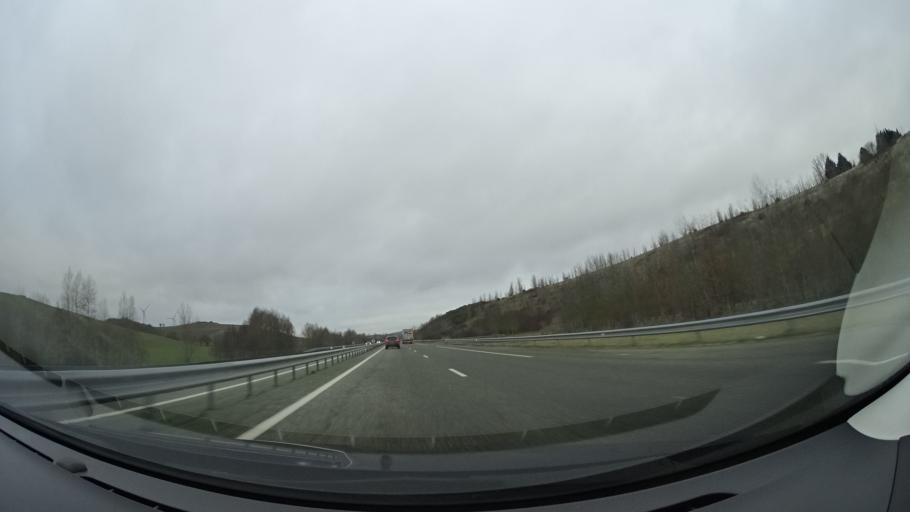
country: FR
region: Midi-Pyrenees
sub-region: Departement de la Haute-Garonne
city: Calmont
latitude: 43.3172
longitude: 1.6442
